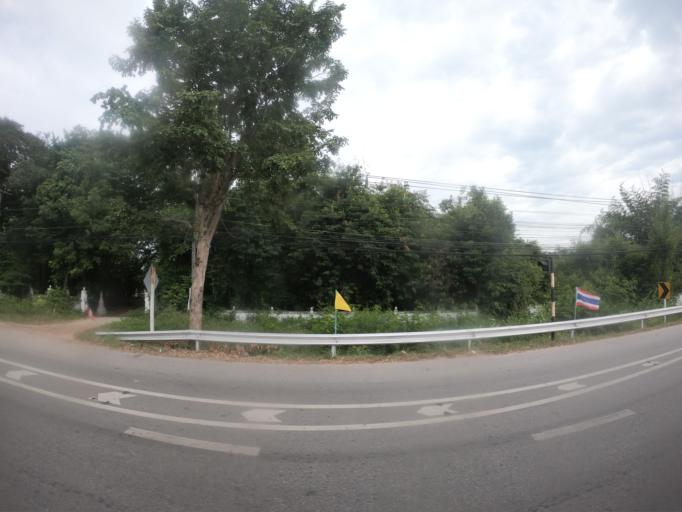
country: TH
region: Maha Sarakham
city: Maha Sarakham
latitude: 16.2011
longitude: 103.2923
